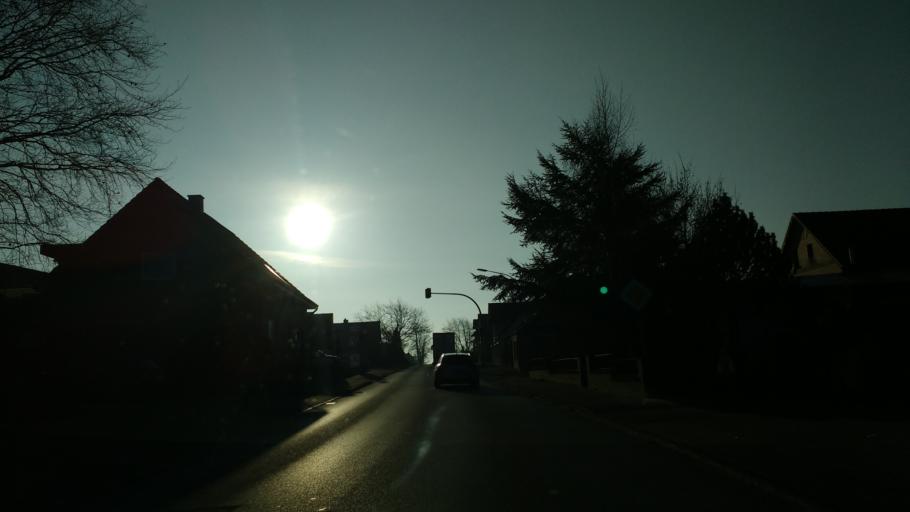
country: DE
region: Schleswig-Holstein
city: Schenefeld
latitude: 54.0441
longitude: 9.4807
